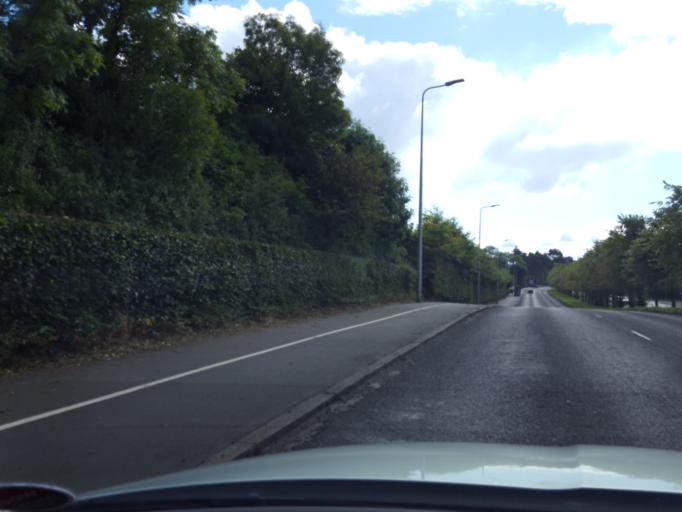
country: GB
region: Scotland
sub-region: Fife
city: Rosyth
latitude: 56.0554
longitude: -3.4383
